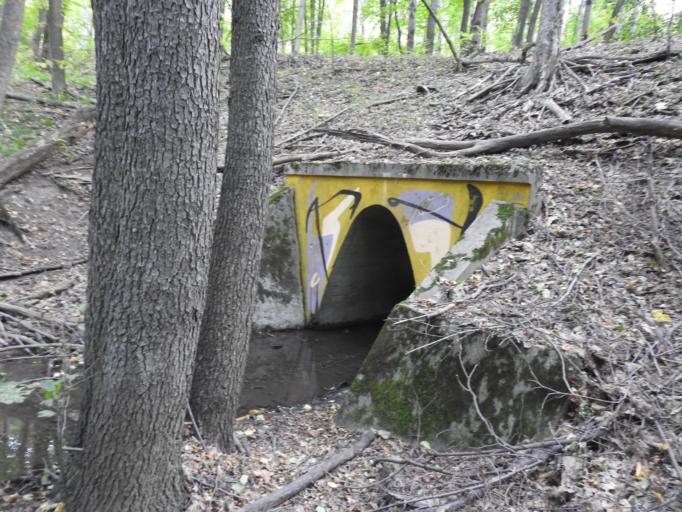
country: RU
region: Saratov
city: Sokolovyy
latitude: 51.5520
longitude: 45.8712
